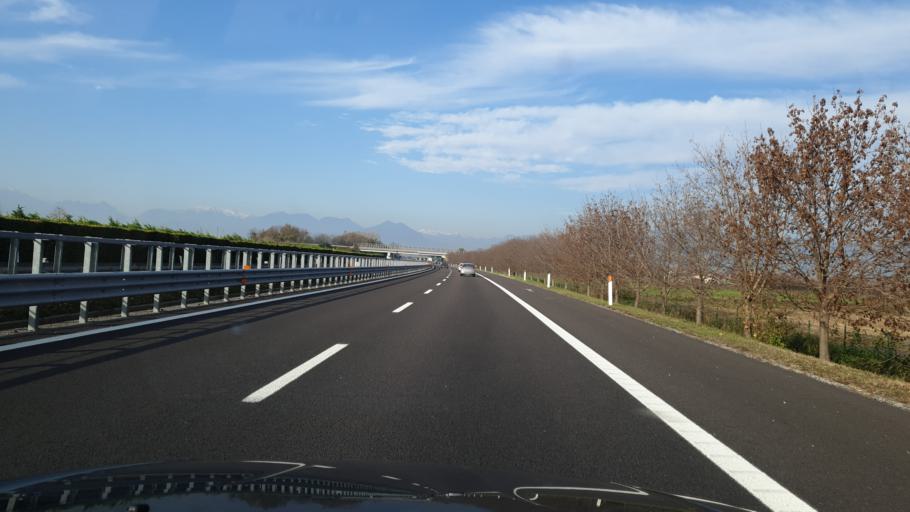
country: IT
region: Veneto
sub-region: Provincia di Vicenza
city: Vigardolo
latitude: 45.6273
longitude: 11.5907
